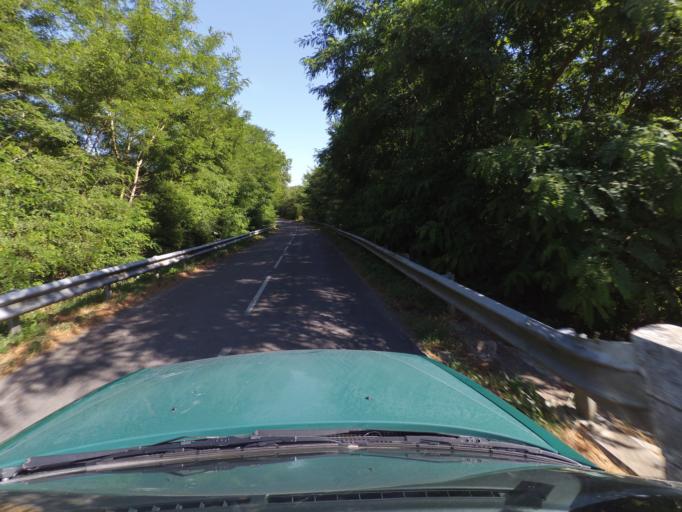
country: FR
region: Pays de la Loire
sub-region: Departement de la Loire-Atlantique
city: Aigrefeuille-sur-Maine
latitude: 47.1082
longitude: -1.4146
